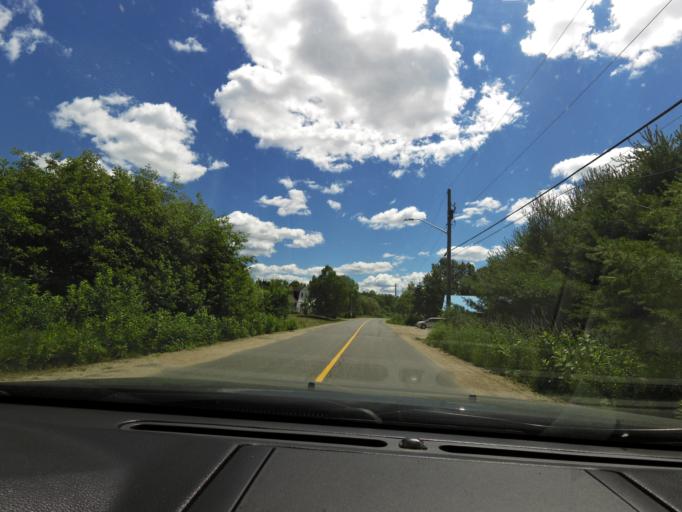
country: CA
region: Ontario
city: Huntsville
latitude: 45.5528
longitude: -79.2249
